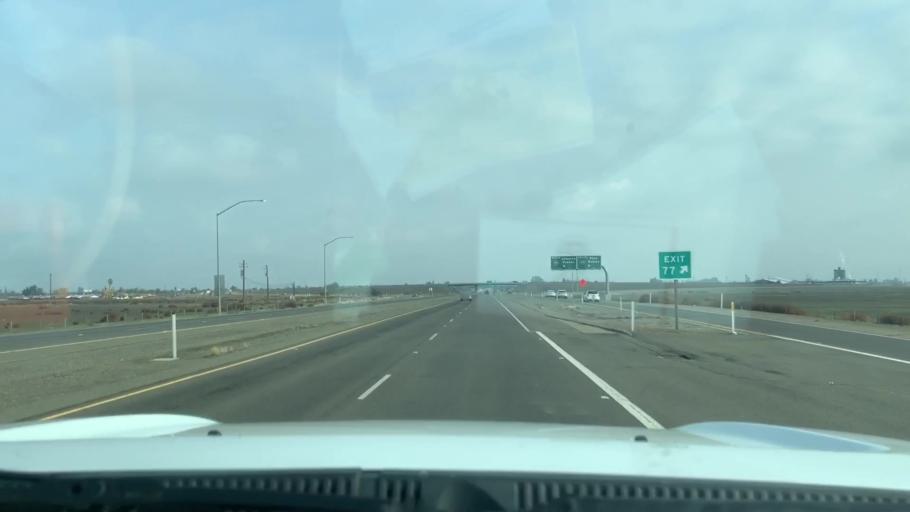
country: US
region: California
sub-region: Kings County
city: Lemoore
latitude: 36.2796
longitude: -119.8139
